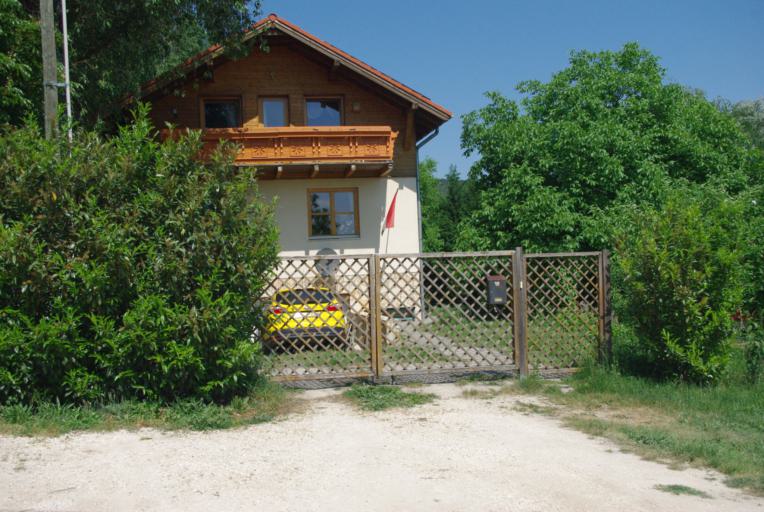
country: HU
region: Pest
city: Pilisborosjeno
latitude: 47.6056
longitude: 18.9878
